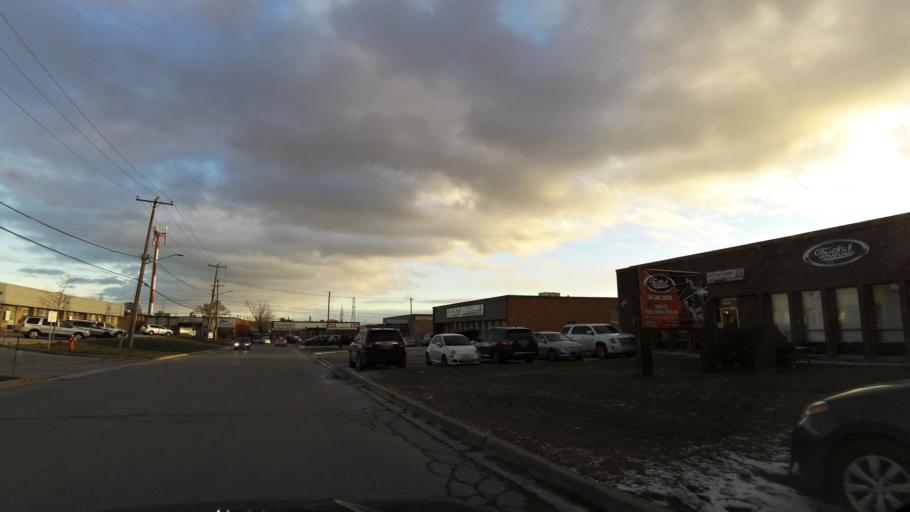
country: CA
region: Ontario
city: Etobicoke
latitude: 43.6319
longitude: -79.6228
